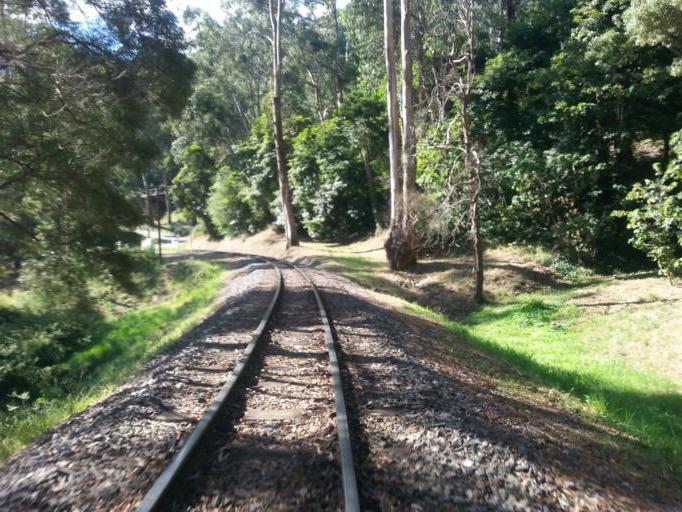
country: AU
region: Victoria
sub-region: Yarra Ranges
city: Selby
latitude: -37.9179
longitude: 145.3807
